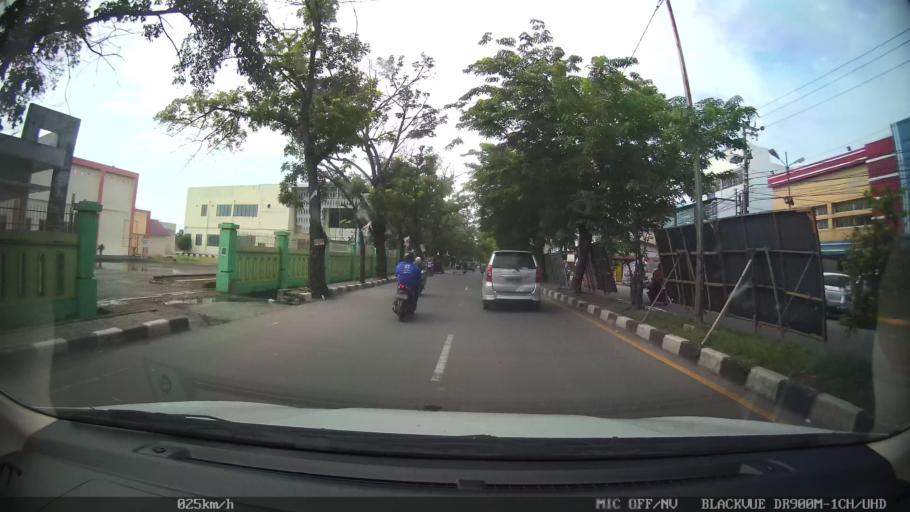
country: ID
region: North Sumatra
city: Medan
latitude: 3.6133
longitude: 98.7071
